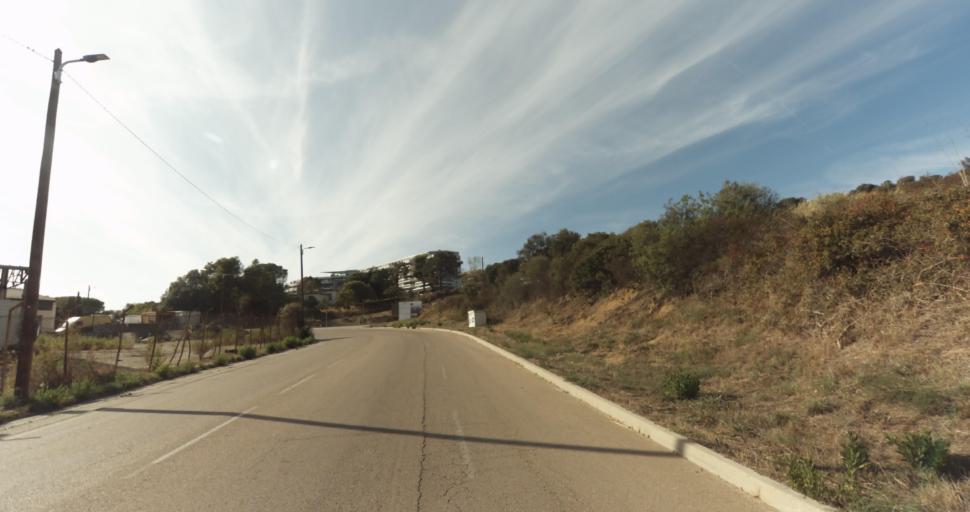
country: FR
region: Corsica
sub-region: Departement de la Corse-du-Sud
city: Ajaccio
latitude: 41.9296
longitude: 8.7659
